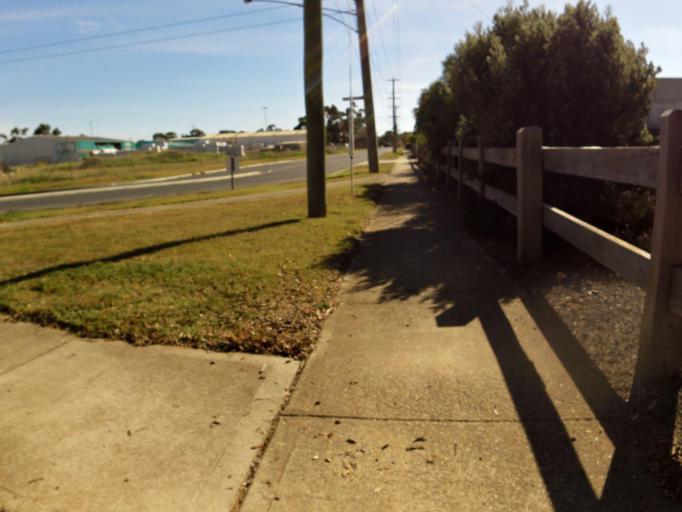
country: AU
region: Victoria
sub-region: Melton
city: Melton
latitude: -37.6884
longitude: 144.5922
